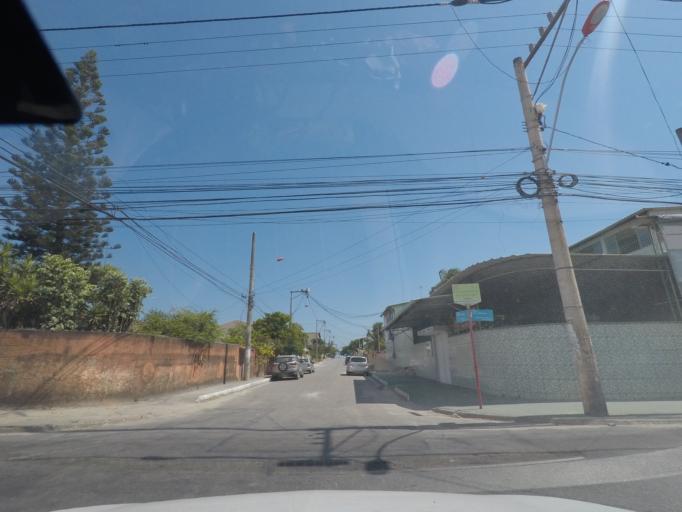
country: BR
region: Rio de Janeiro
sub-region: Marica
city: Marica
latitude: -22.9646
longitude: -42.9631
